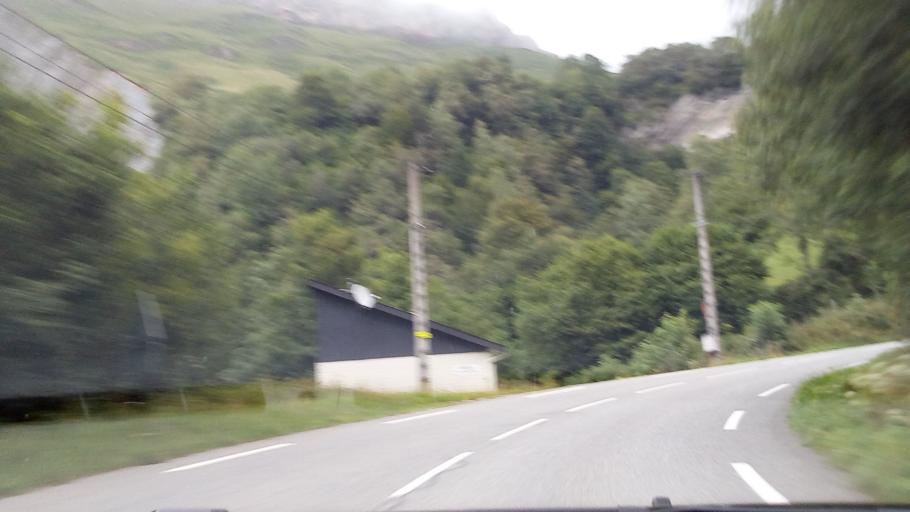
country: FR
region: Aquitaine
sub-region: Departement des Pyrenees-Atlantiques
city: Laruns
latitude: 42.9689
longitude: -0.3726
